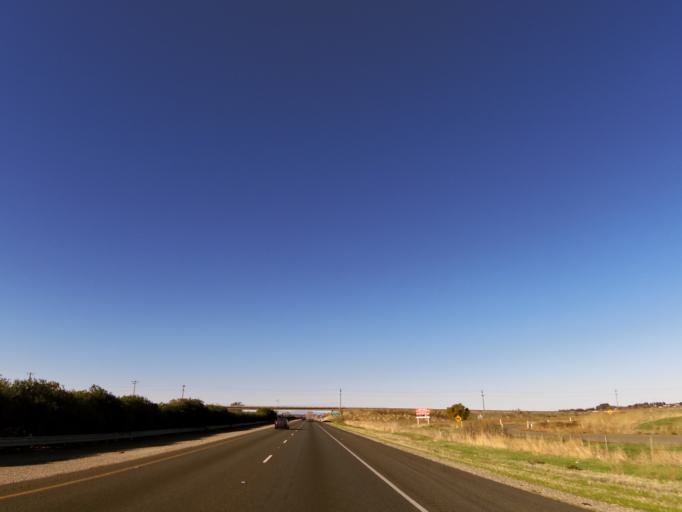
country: US
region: California
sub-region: Yolo County
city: West Sacramento
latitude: 38.6714
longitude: -121.5735
